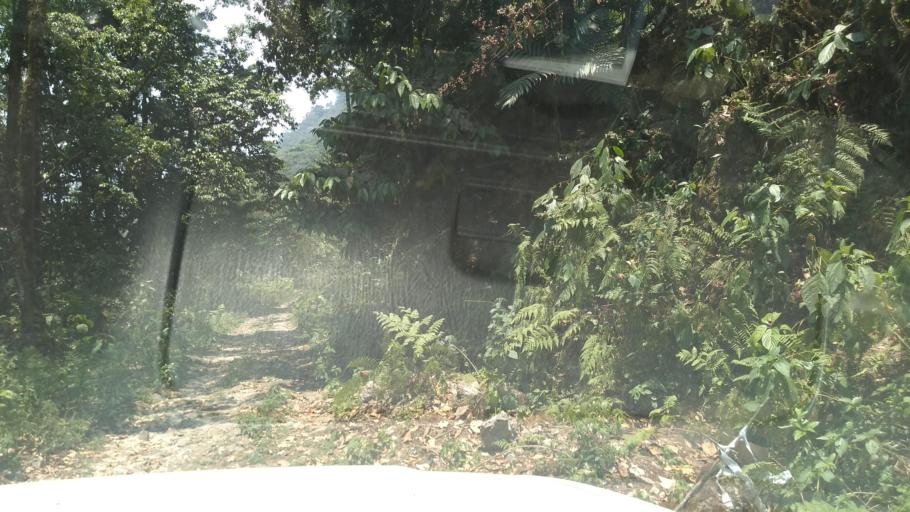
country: MX
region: Veracruz
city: Motzorongo
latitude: 18.6070
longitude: -96.7591
